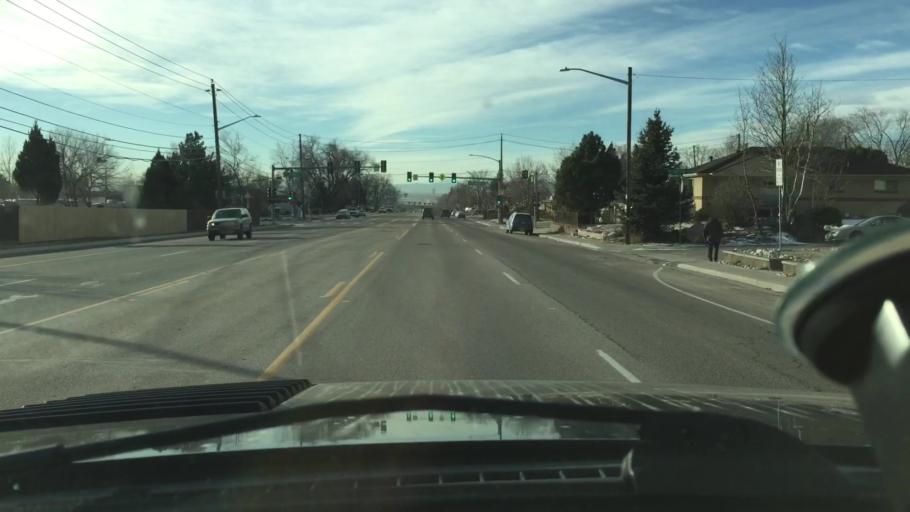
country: US
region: Colorado
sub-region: Adams County
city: Sherrelwood
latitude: 39.8391
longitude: -105.0061
